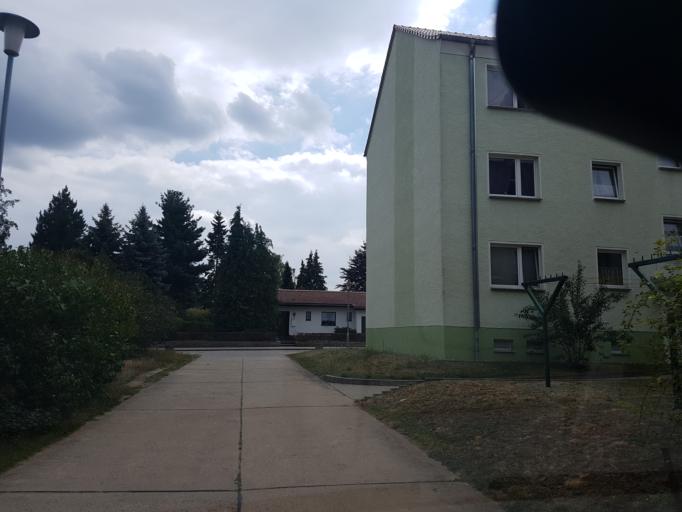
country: DE
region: Brandenburg
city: Treuenbrietzen
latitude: 52.0899
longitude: 12.8519
